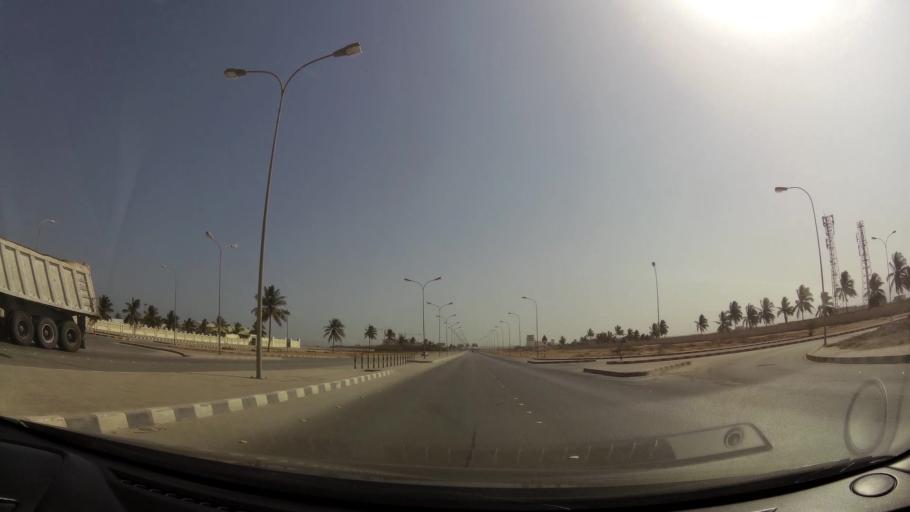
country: OM
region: Zufar
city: Salalah
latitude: 16.9901
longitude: 54.0252
